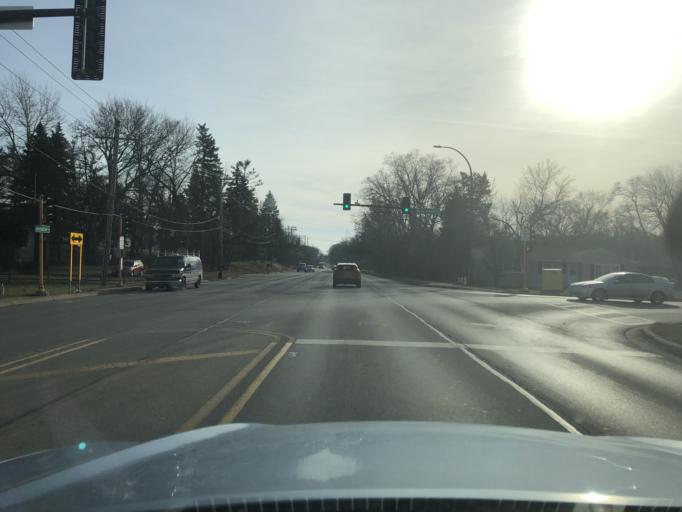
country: US
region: Illinois
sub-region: DuPage County
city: Roselle
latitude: 41.9765
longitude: -88.0804
